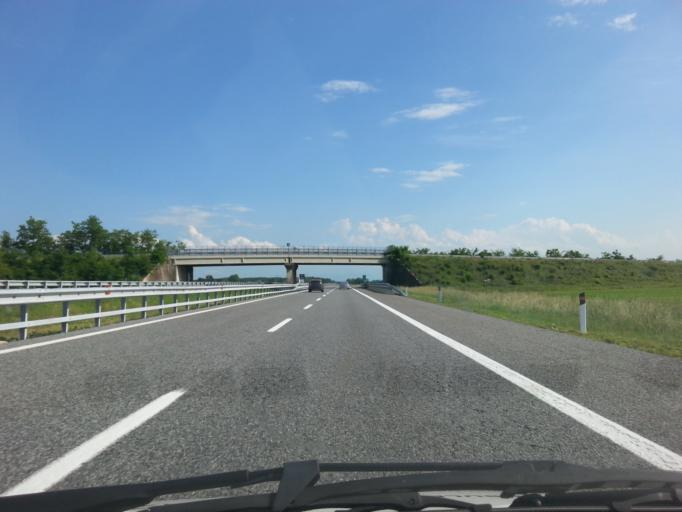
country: IT
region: Piedmont
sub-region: Provincia di Cuneo
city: Sommariva del Bosco
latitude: 44.7363
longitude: 7.7537
